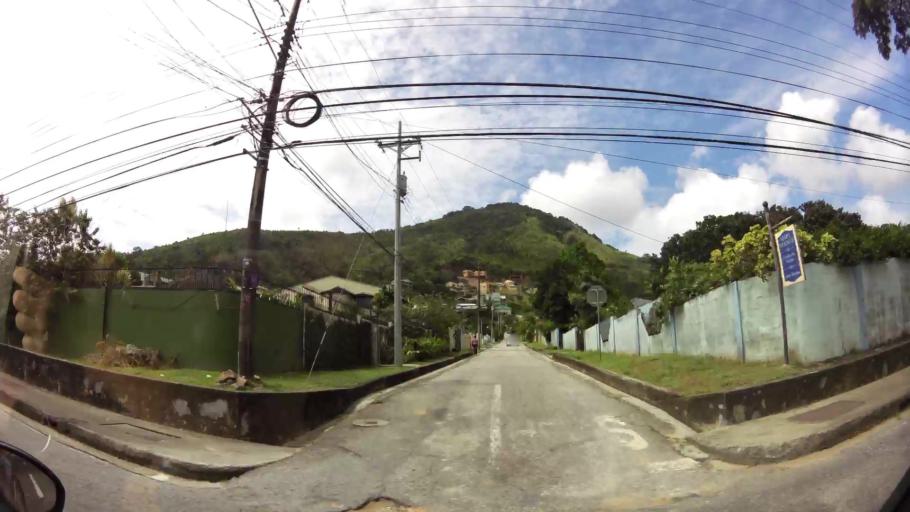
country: TT
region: Diego Martin
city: Petit Valley
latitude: 10.7028
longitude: -61.5558
